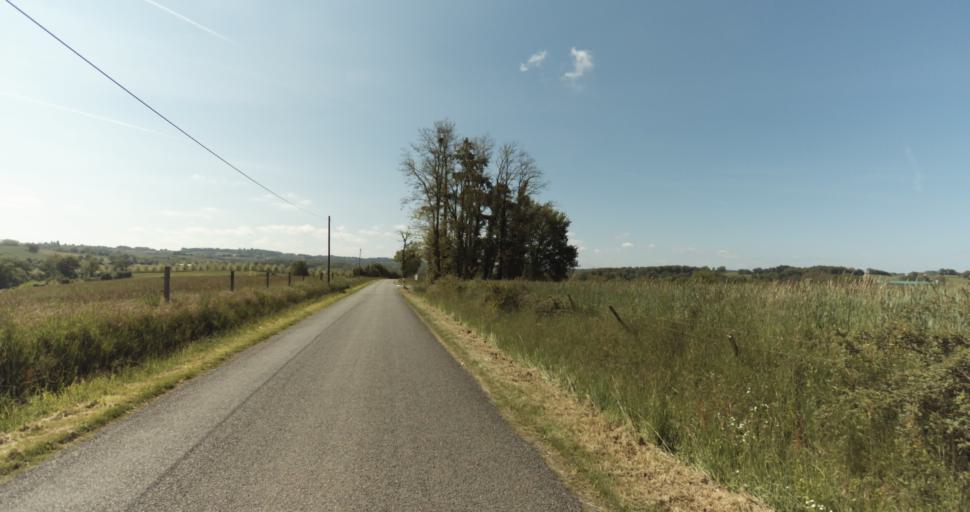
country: FR
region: Limousin
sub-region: Departement de la Haute-Vienne
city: Le Vigen
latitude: 45.7025
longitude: 1.3022
